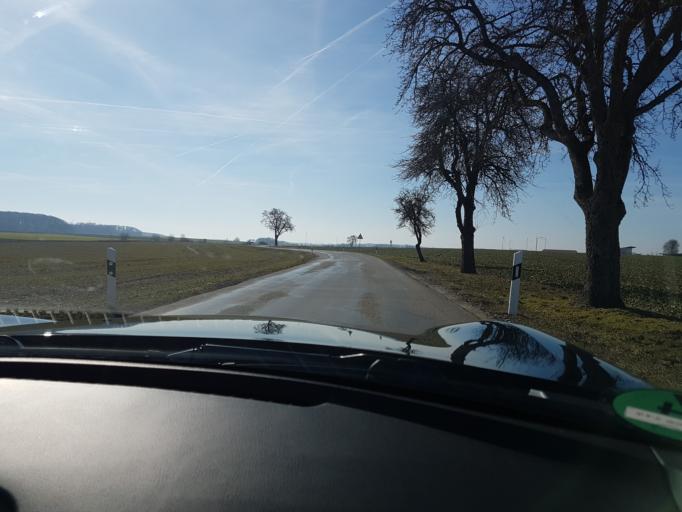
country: DE
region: Baden-Wuerttemberg
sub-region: Regierungsbezirk Stuttgart
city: Langenburg
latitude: 49.2634
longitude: 9.8826
